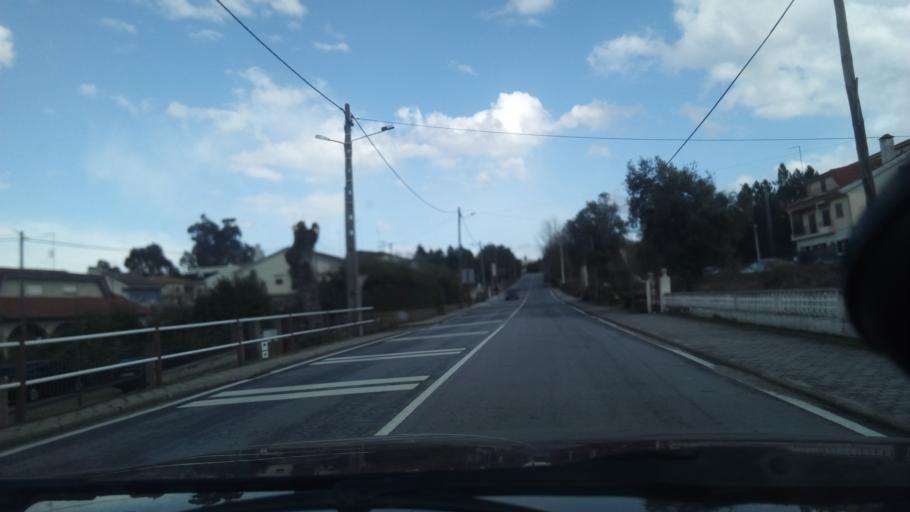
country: PT
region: Guarda
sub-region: Celorico da Beira
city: Celorico da Beira
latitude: 40.6263
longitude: -7.3351
